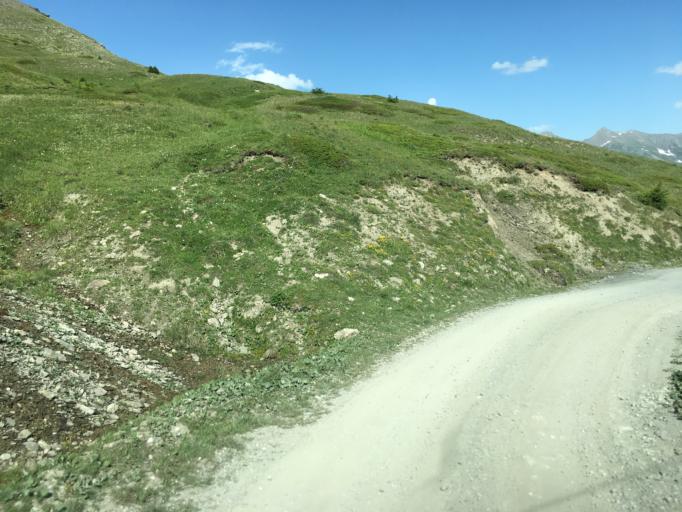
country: IT
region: Piedmont
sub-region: Provincia di Torino
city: Sestriere
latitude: 44.9802
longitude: 6.8753
